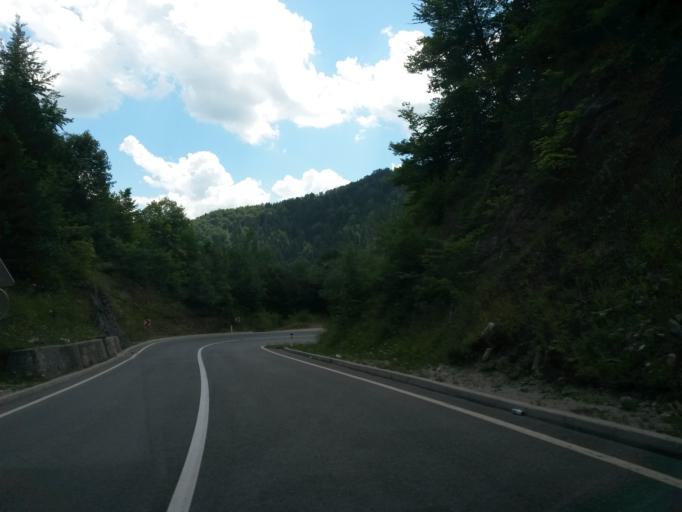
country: BA
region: Federation of Bosnia and Herzegovina
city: Bugojno
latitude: 44.0276
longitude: 17.3574
